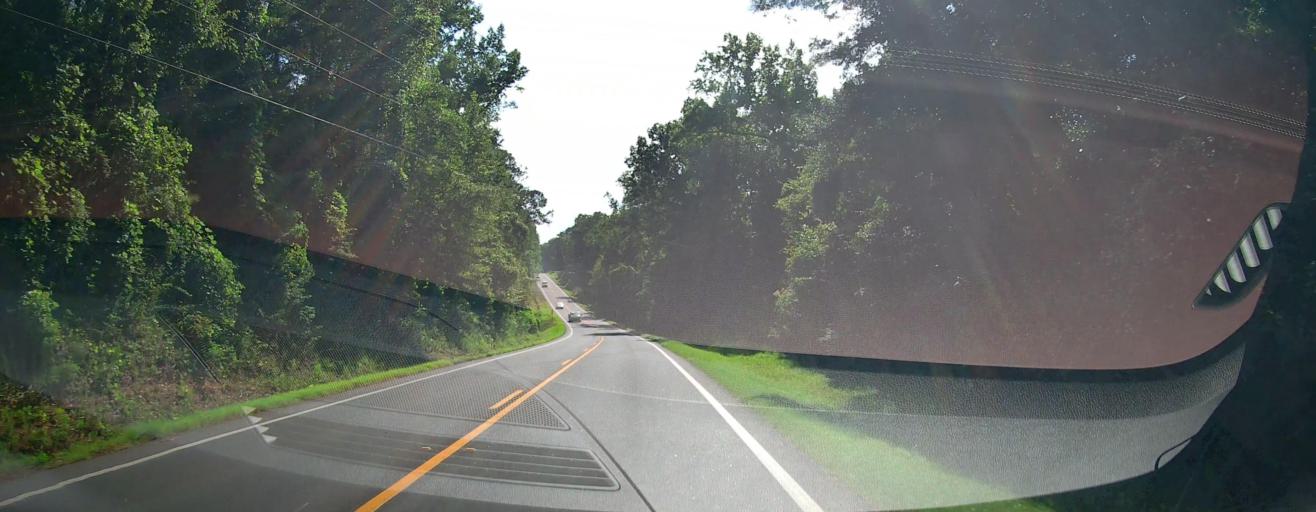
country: US
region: Georgia
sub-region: Upson County
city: Hannahs Mill
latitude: 32.9058
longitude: -84.3729
